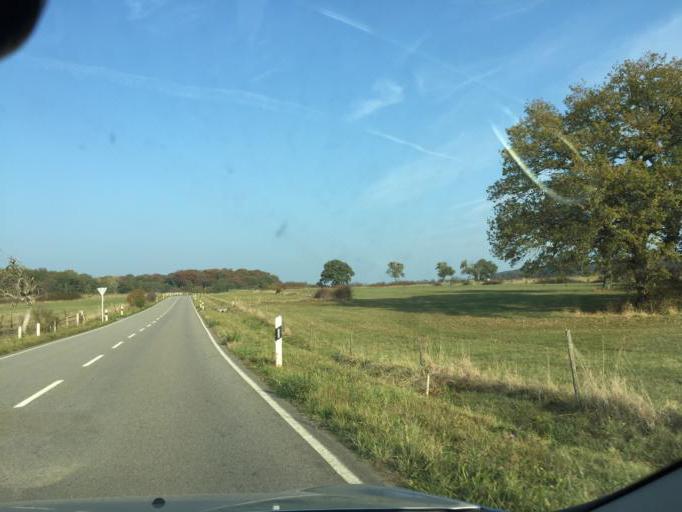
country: LU
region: Luxembourg
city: Aspelt
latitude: 49.5470
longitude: 6.2328
